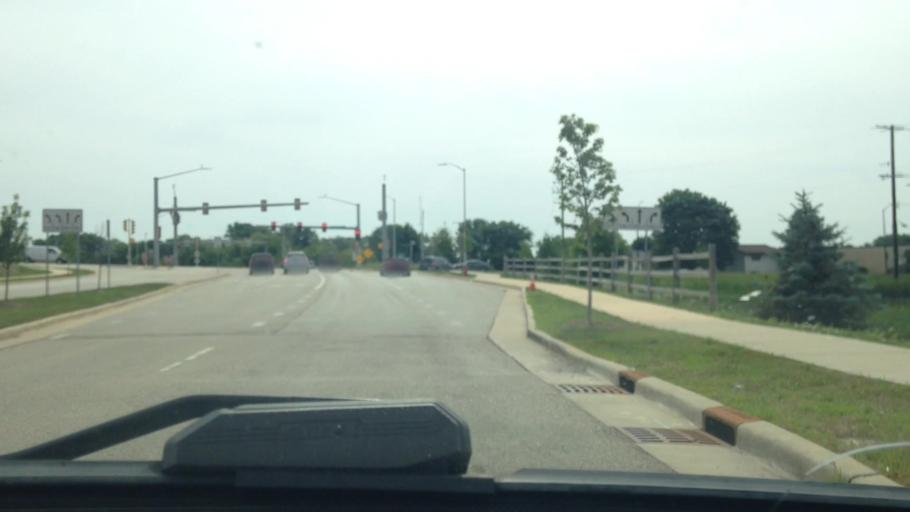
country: US
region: Wisconsin
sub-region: Waukesha County
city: Menomonee Falls
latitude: 43.1814
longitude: -88.1046
